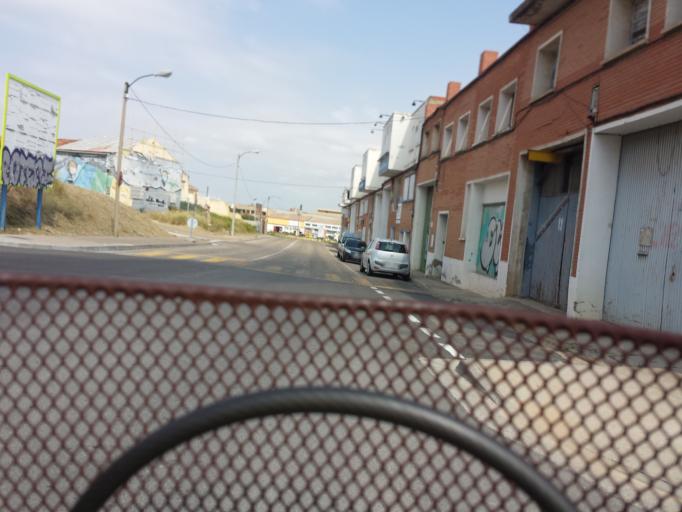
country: ES
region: Aragon
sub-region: Provincia de Zaragoza
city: Oliver-Valdefierro, Oliver, Valdefierro
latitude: 41.6409
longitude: -0.9253
